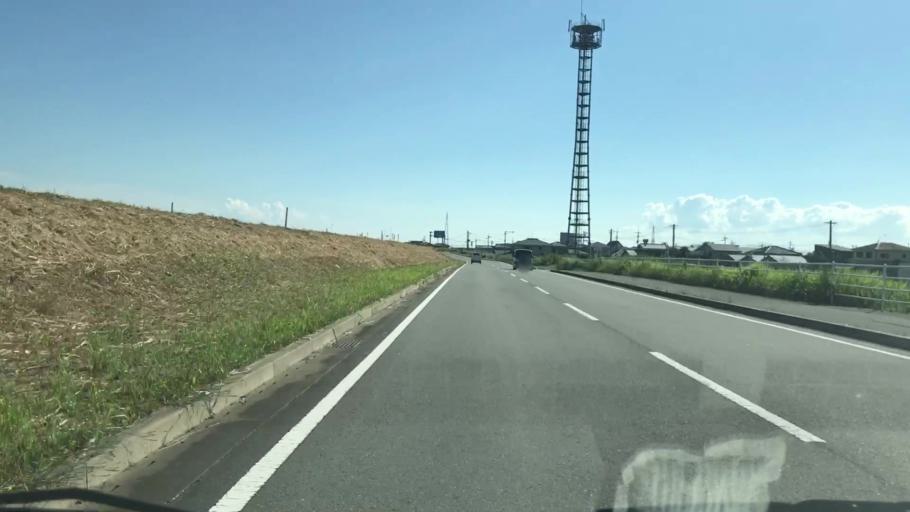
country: JP
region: Saga Prefecture
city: Okawa
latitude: 33.2398
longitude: 130.3817
